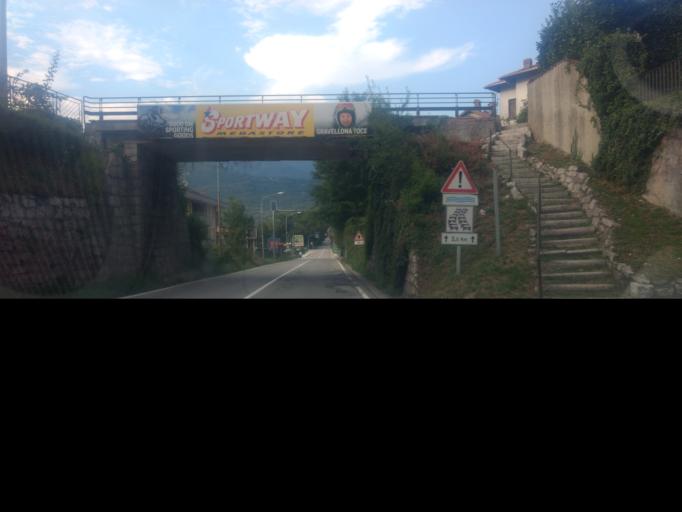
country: IT
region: Piedmont
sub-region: Provincia Verbano-Cusio-Ossola
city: Baveno
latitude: 45.9308
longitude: 8.4794
